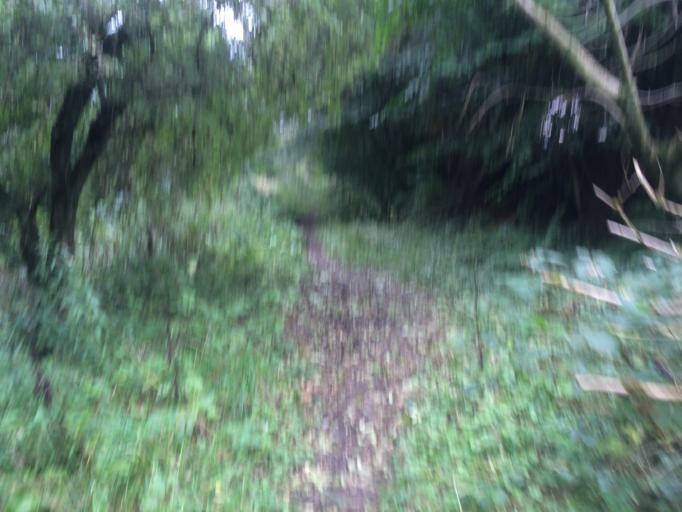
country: GB
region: Scotland
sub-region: East Dunbartonshire
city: Bishopbriggs
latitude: 55.9160
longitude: -4.2393
